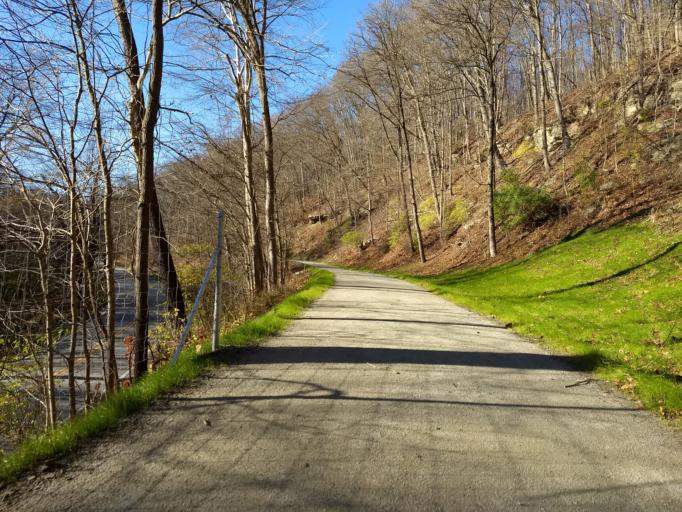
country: US
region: Pennsylvania
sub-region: Washington County
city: Gastonville
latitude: 40.2769
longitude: -79.9720
